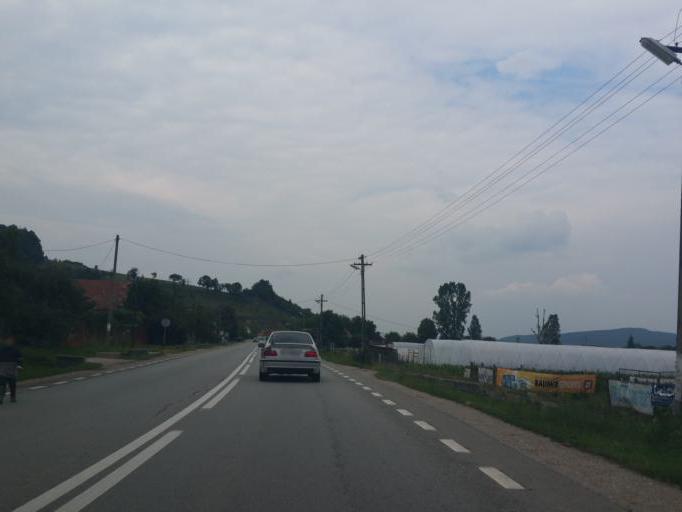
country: RO
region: Salaj
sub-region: Comuna Zimbor
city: Zimbor
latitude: 46.9976
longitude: 23.2523
